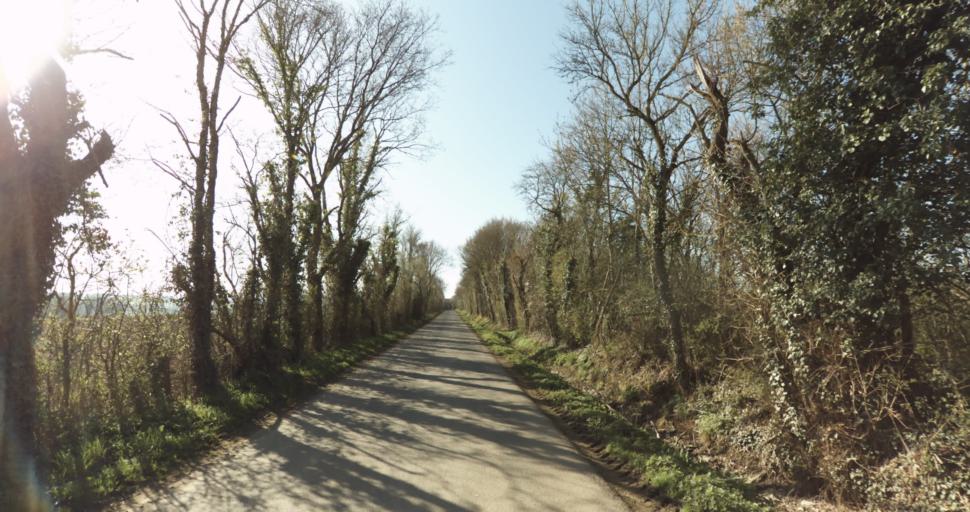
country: FR
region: Lower Normandy
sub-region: Departement du Calvados
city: Saint-Pierre-sur-Dives
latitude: 48.9961
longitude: -0.0031
